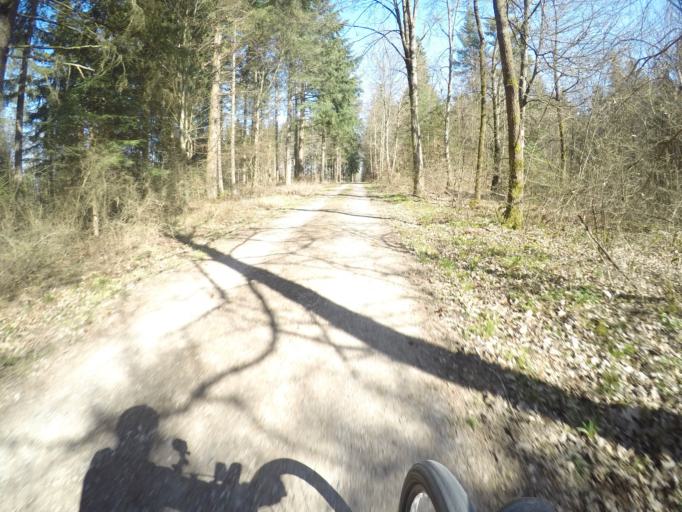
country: DE
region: Baden-Wuerttemberg
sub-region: Regierungsbezirk Stuttgart
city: Deckenpfronn
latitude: 48.6746
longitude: 8.8145
